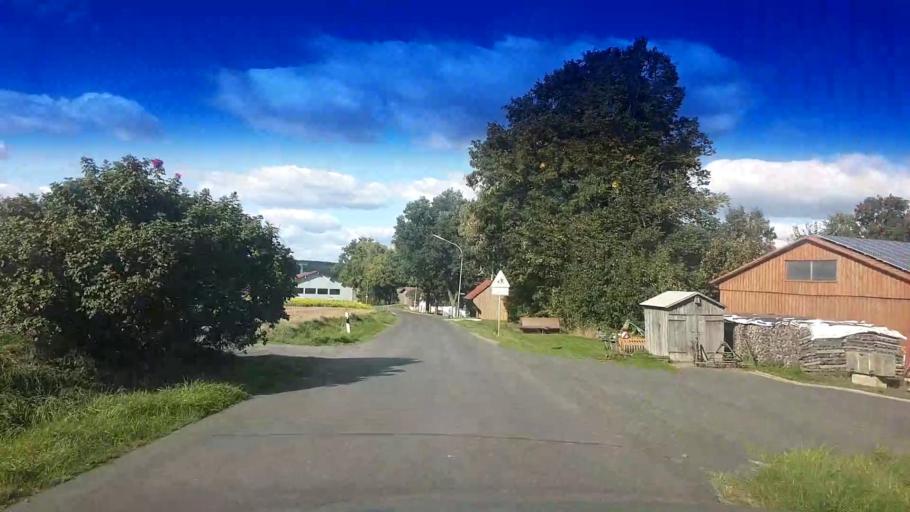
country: DE
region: Bavaria
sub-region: Upper Franconia
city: Schirnding
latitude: 50.0250
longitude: 12.2350
